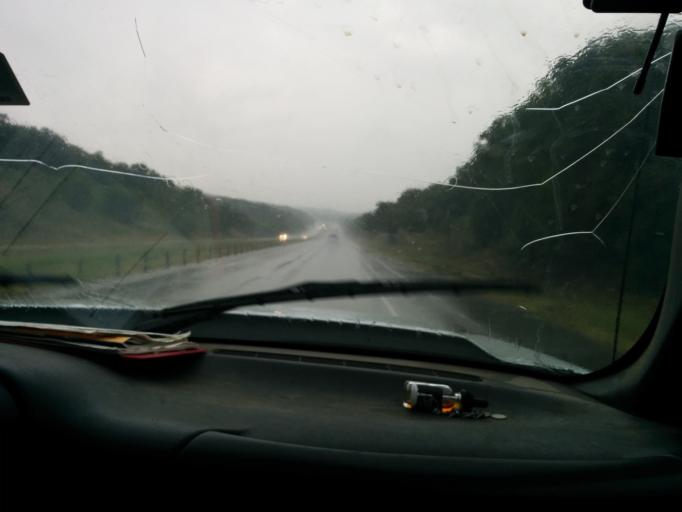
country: US
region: Oklahoma
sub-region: Okmulgee County
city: Beggs
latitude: 35.7278
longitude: -96.0024
